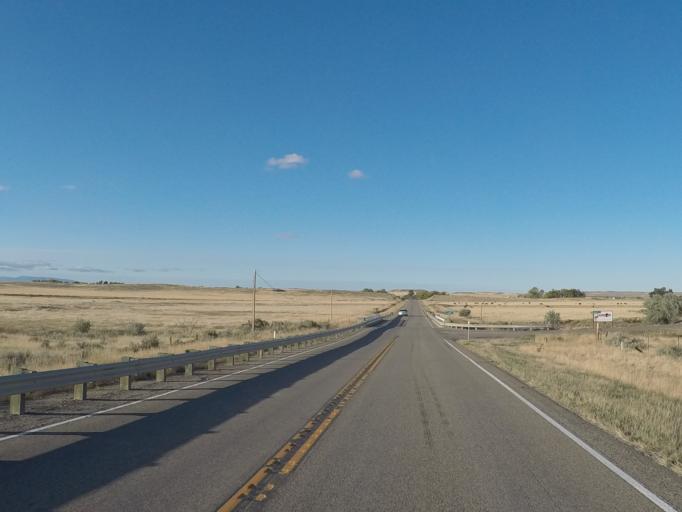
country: US
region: Montana
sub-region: Golden Valley County
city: Ryegate
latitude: 46.2794
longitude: -108.9397
